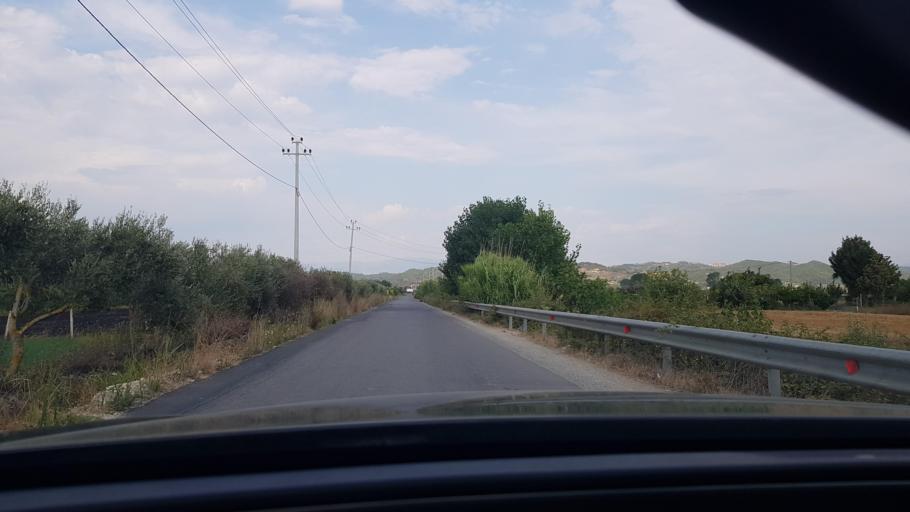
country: AL
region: Durres
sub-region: Rrethi i Durresit
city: Manze
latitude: 41.4725
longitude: 19.5420
